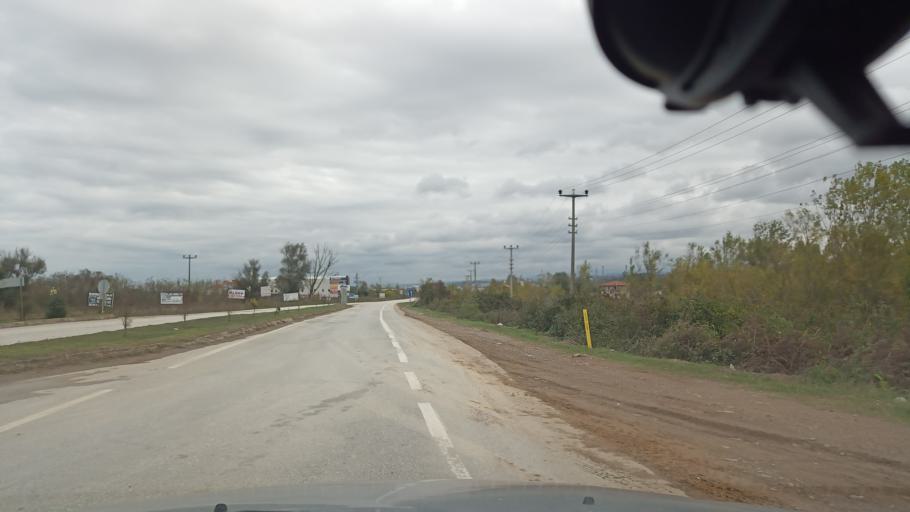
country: TR
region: Sakarya
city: Karasu
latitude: 41.1171
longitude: 30.6510
